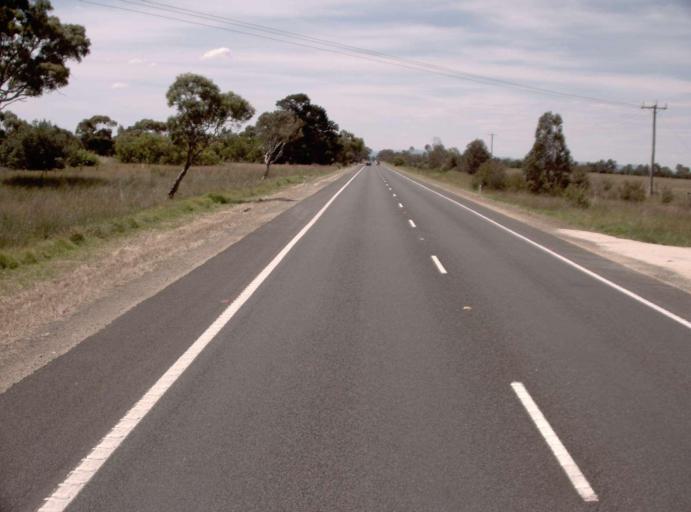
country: AU
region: Victoria
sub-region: Wellington
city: Sale
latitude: -38.0109
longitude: 147.0620
